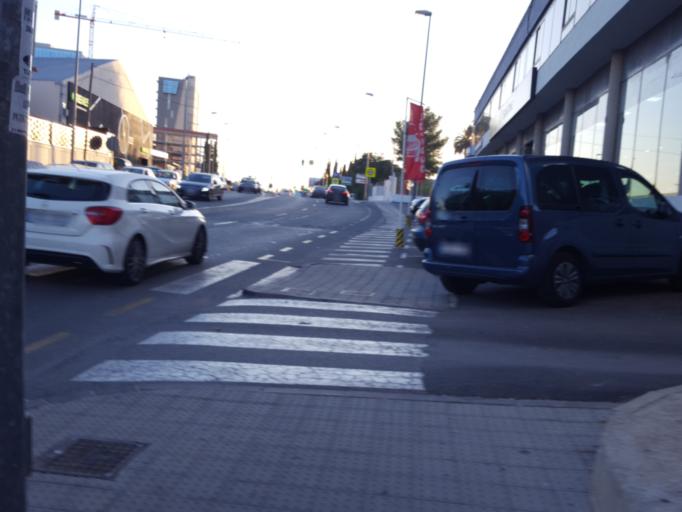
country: ES
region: Murcia
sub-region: Murcia
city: Murcia
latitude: 38.0032
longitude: -1.1470
